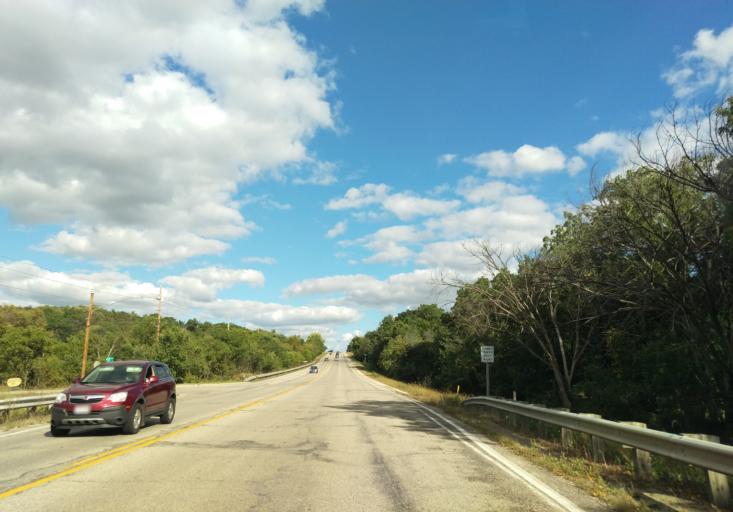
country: US
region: Wisconsin
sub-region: Rock County
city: Janesville
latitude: 42.7301
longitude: -89.0576
